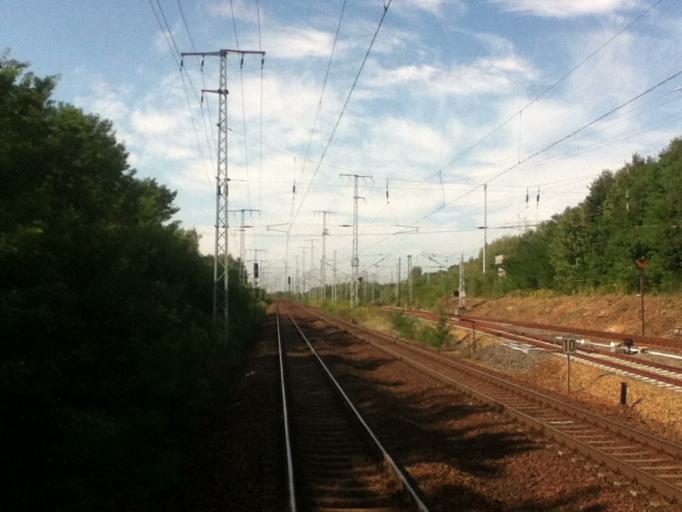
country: DE
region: Brandenburg
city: Senftenberg
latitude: 51.5452
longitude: 14.0395
